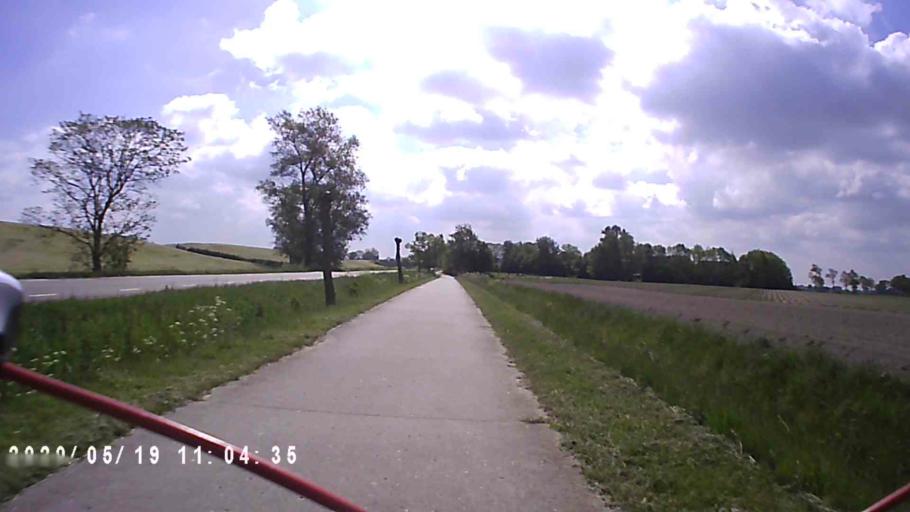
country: NL
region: Groningen
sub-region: Gemeente Zuidhorn
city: Grijpskerk
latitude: 53.2969
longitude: 6.2856
